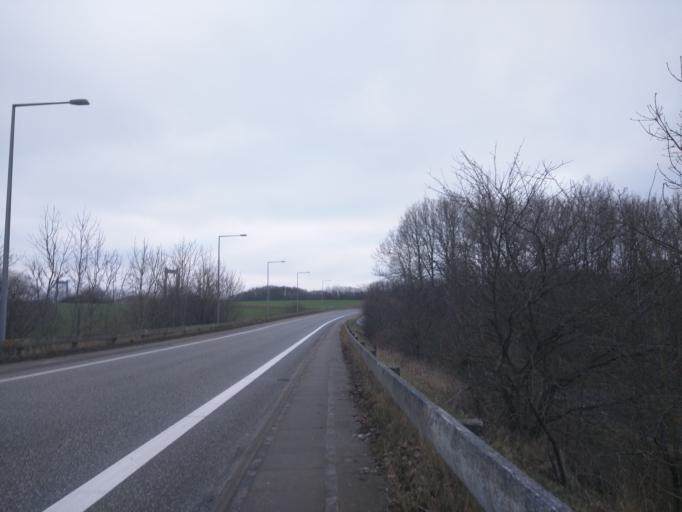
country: DK
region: South Denmark
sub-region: Fredericia Kommune
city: Snoghoj
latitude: 55.5288
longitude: 9.7315
